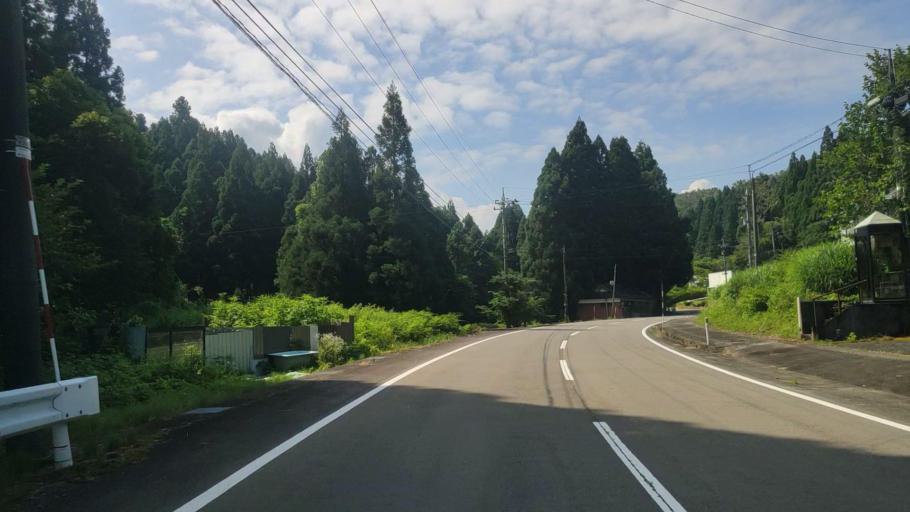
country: JP
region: Ishikawa
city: Komatsu
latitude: 36.3047
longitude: 136.5280
